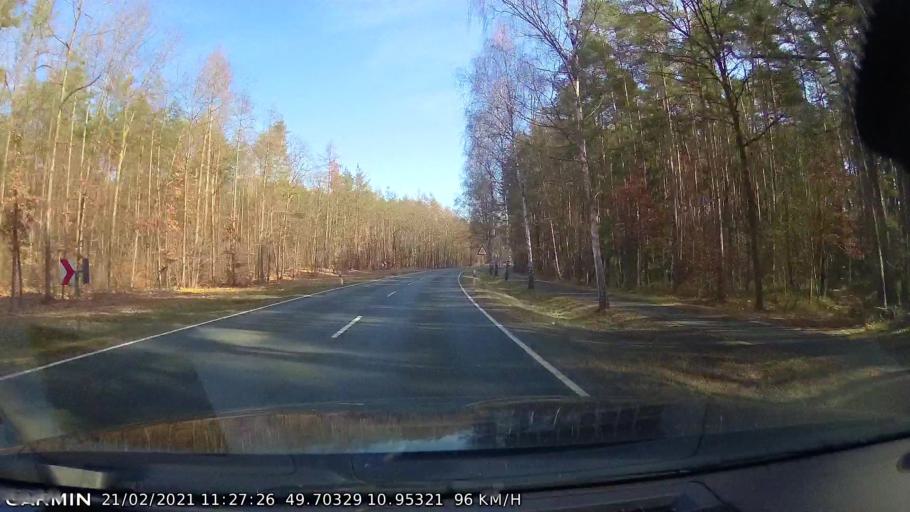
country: DE
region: Bavaria
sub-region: Regierungsbezirk Mittelfranken
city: Hemhofen
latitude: 49.7034
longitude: 10.9535
